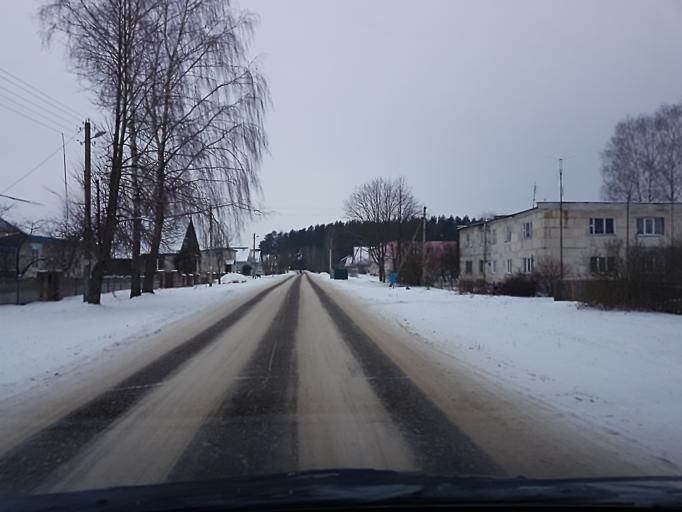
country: BY
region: Minsk
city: Rakaw
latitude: 53.9578
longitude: 27.0618
